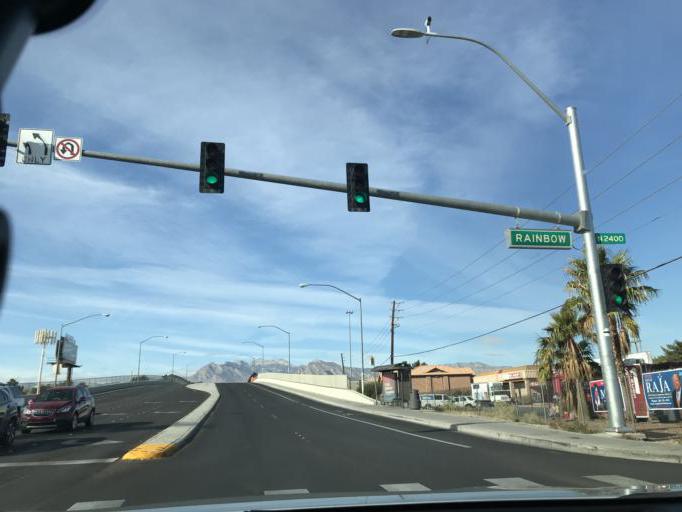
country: US
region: Nevada
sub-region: Clark County
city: Spring Valley
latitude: 36.2034
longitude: -115.2424
